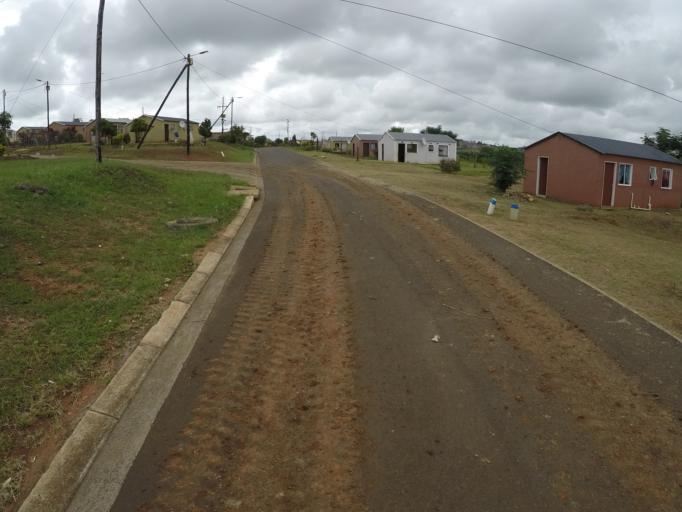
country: ZA
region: KwaZulu-Natal
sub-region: uThungulu District Municipality
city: Empangeni
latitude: -28.7644
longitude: 31.8826
